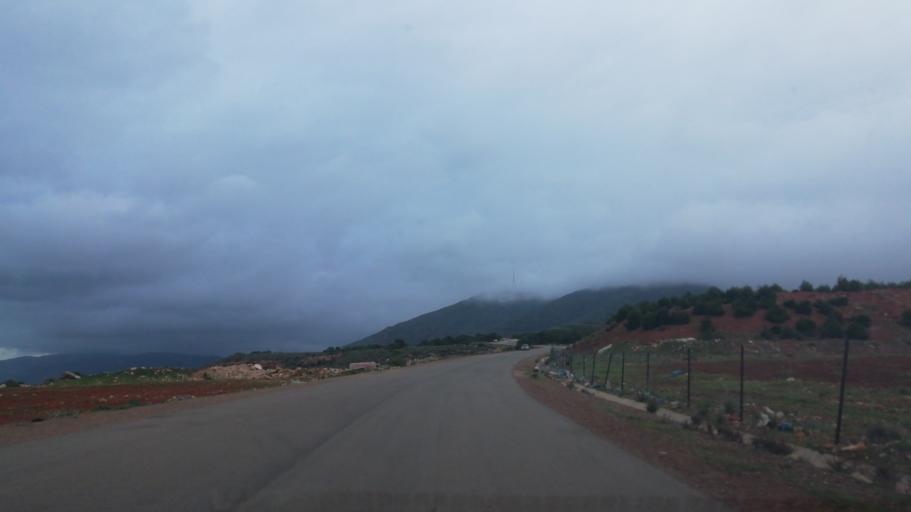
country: DZ
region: Oran
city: Bir el Djir
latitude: 35.7624
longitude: -0.5238
